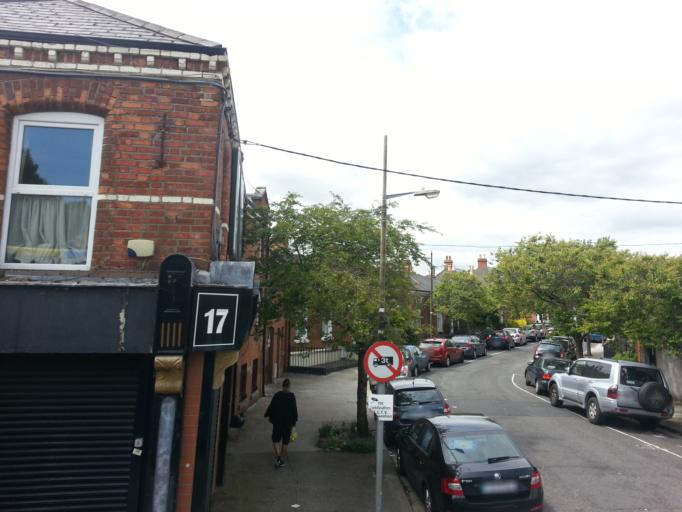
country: IE
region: Leinster
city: Drumcondra
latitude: 53.3589
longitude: -6.2697
